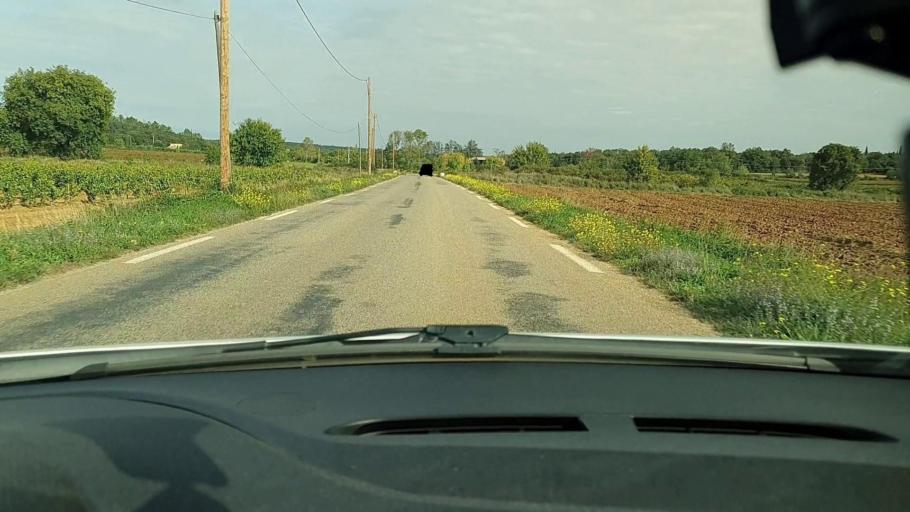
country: FR
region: Languedoc-Roussillon
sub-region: Departement du Gard
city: Saint-Quentin-la-Poterie
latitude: 44.0930
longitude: 4.4557
